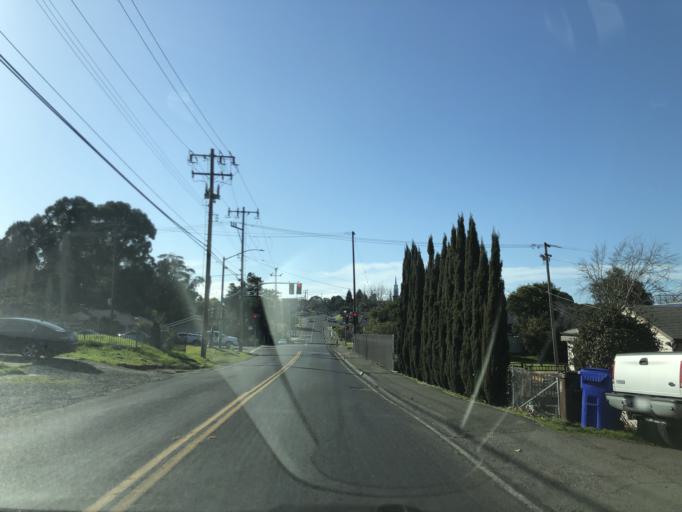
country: US
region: California
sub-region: Contra Costa County
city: El Sobrante
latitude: 37.9771
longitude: -122.3073
